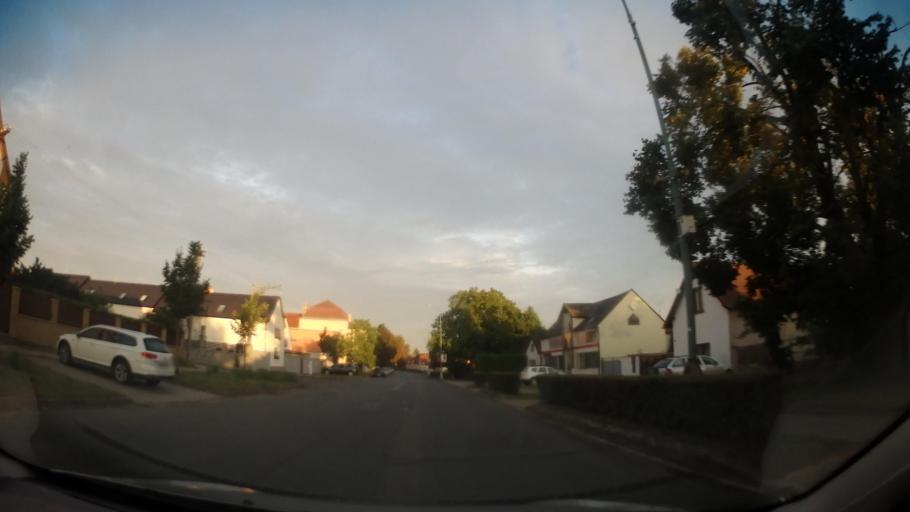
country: CZ
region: Central Bohemia
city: Milovice
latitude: 50.2268
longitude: 14.8869
